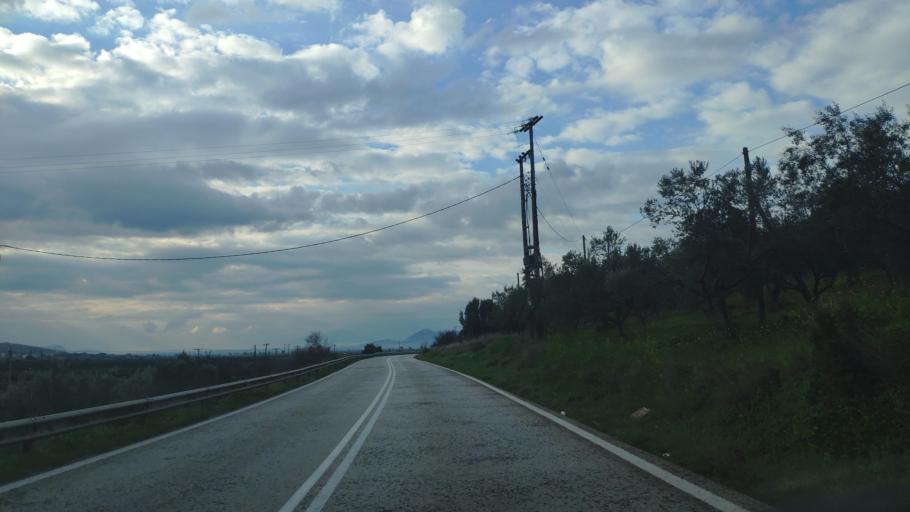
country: GR
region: Peloponnese
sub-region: Nomos Argolidos
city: Koutsopodi
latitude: 37.7351
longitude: 22.7361
